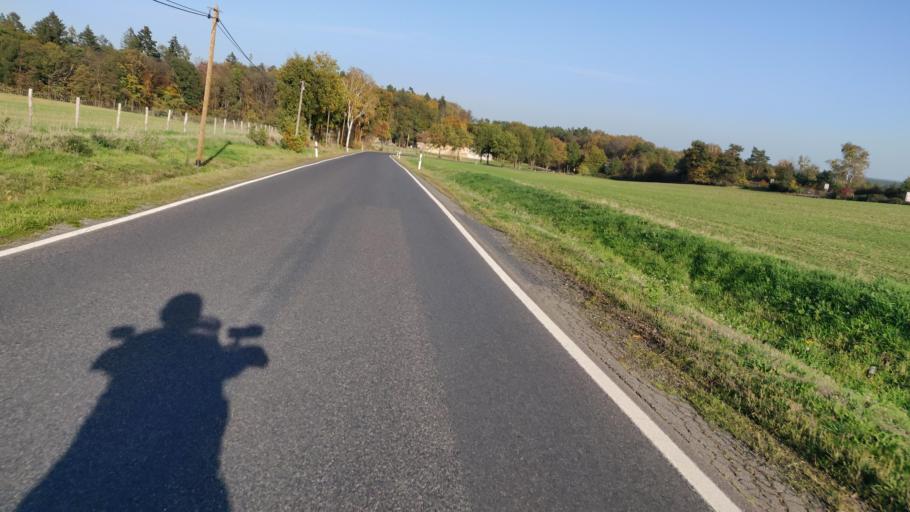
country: DE
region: Brandenburg
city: Grosskmehlen
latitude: 51.3642
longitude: 13.7376
